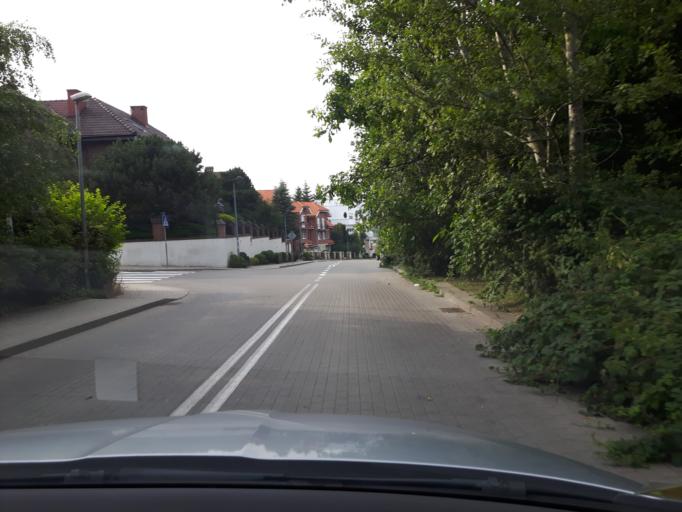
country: PL
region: Pomeranian Voivodeship
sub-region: Gdynia
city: Gdynia
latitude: 54.5024
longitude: 18.5475
